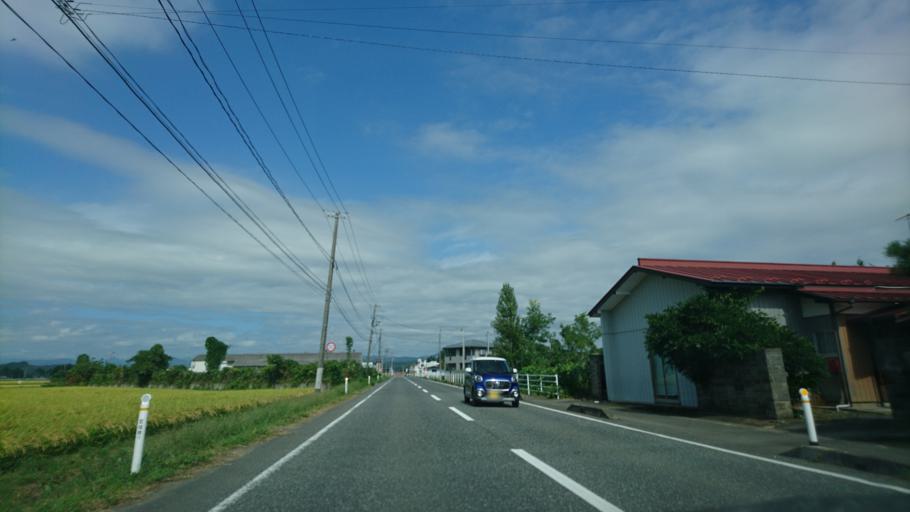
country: JP
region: Miyagi
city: Furukawa
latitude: 38.7370
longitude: 140.9512
